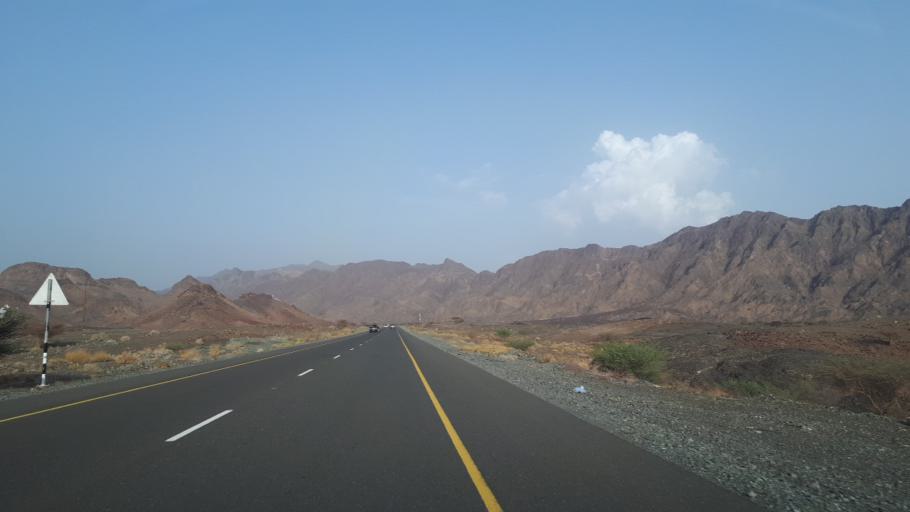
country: OM
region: Az Zahirah
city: Yanqul
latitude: 23.4961
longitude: 56.8565
